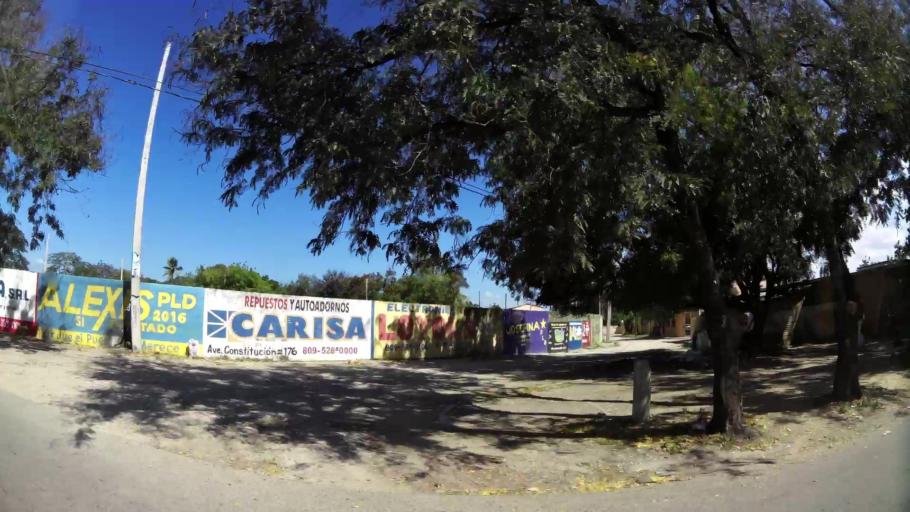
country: DO
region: San Cristobal
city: San Cristobal
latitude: 18.4289
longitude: -70.1268
